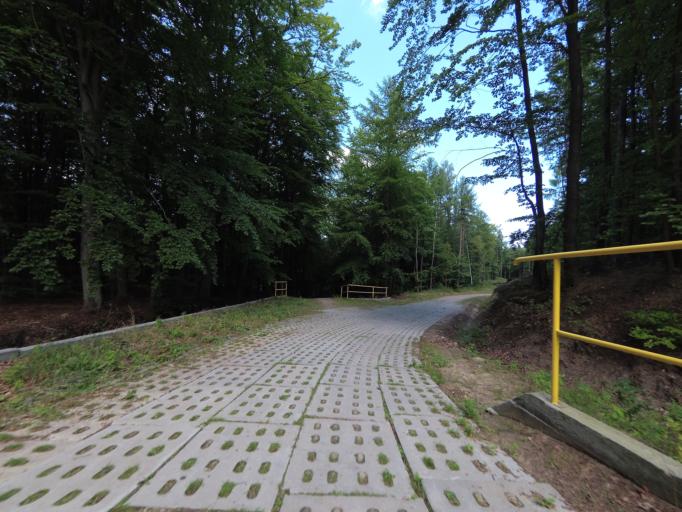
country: PL
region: Pomeranian Voivodeship
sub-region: Gdynia
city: Wielki Kack
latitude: 54.4815
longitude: 18.5012
